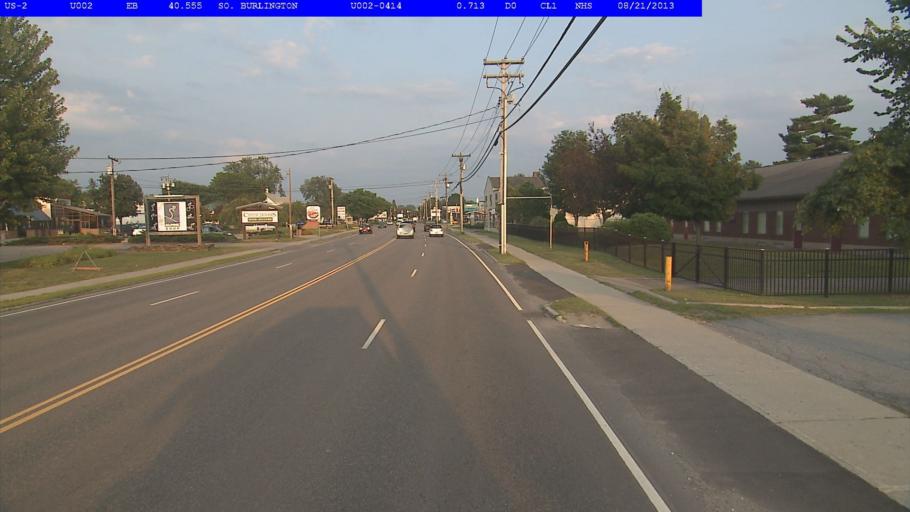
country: US
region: Vermont
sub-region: Chittenden County
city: South Burlington
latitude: 44.4681
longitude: -73.1772
